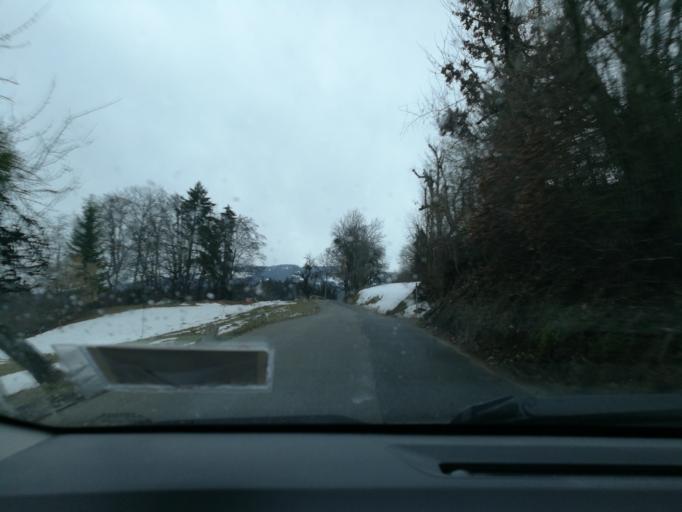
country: FR
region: Rhone-Alpes
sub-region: Departement de la Haute-Savoie
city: Combloux
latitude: 45.9107
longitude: 6.6319
